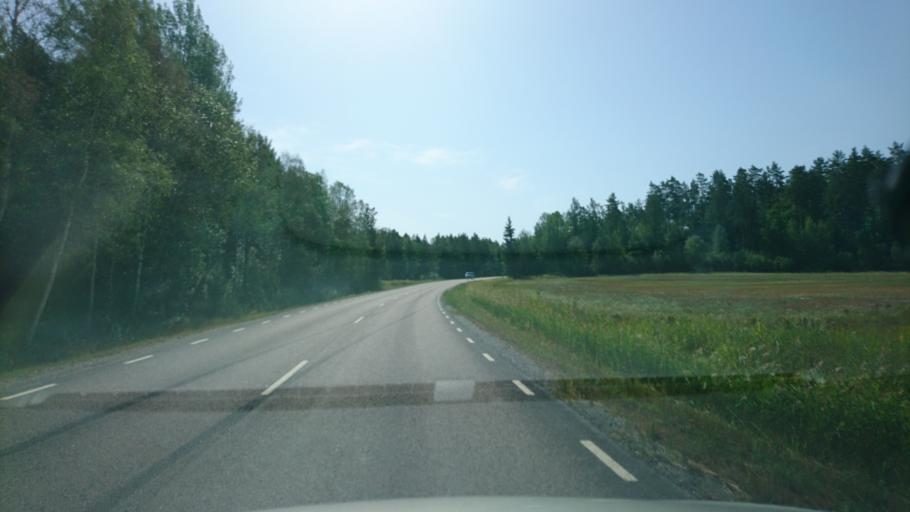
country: SE
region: Soedermanland
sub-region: Strangnas Kommun
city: Strangnas
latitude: 59.4073
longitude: 17.0253
